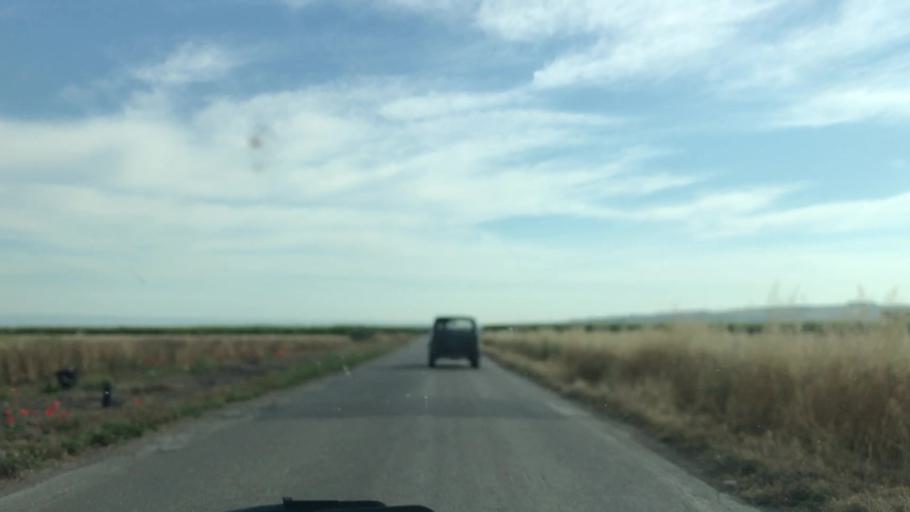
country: IT
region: Apulia
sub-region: Provincia di Taranto
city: San Giorgio Ionico
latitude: 40.4337
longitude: 17.3457
